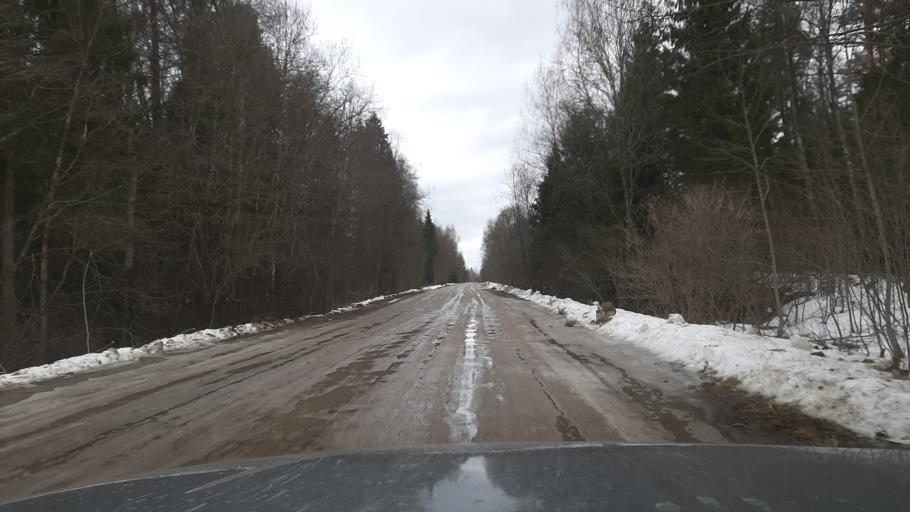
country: RU
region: Ivanovo
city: Teykovo
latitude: 56.8876
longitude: 40.6555
